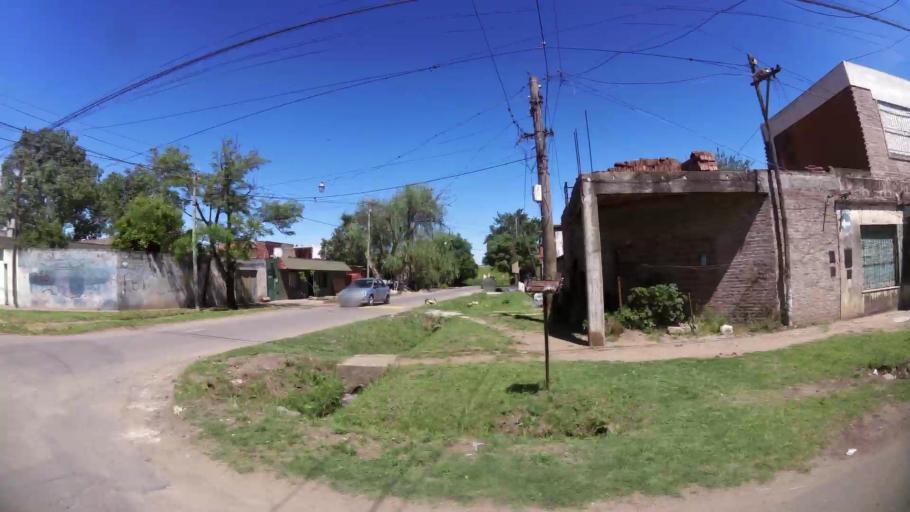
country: AR
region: Santa Fe
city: Perez
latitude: -32.9558
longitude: -60.7201
